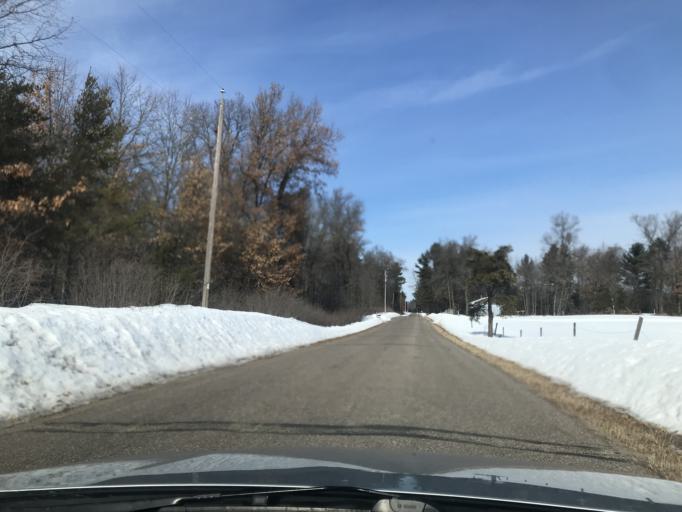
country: US
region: Wisconsin
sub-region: Marinette County
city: Peshtigo
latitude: 45.2211
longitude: -87.9628
